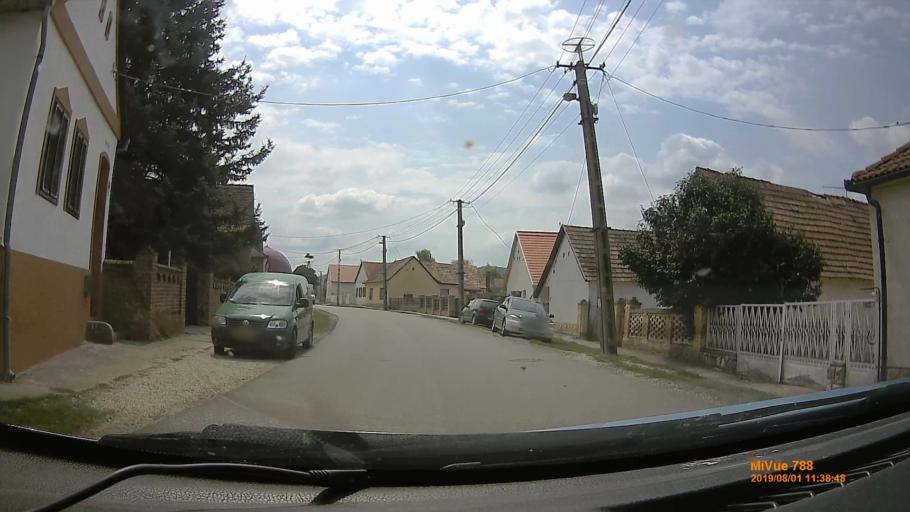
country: HU
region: Baranya
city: Villany
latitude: 45.8973
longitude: 18.3893
